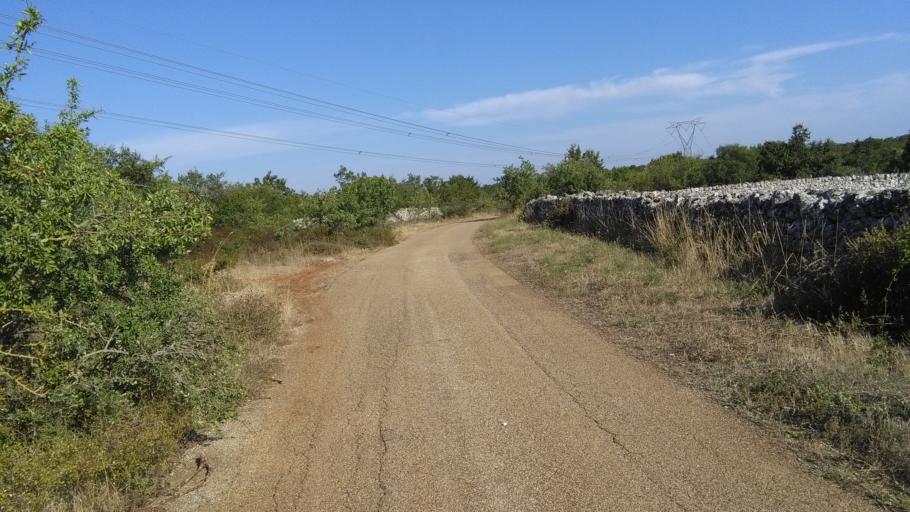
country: IT
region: Apulia
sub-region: Provincia di Bari
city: Putignano
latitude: 40.8184
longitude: 17.0556
